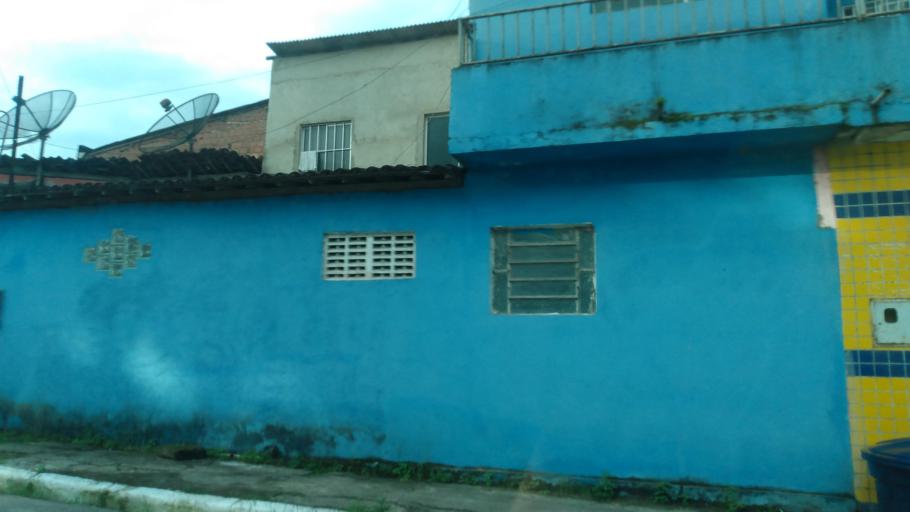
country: BR
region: Pernambuco
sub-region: Palmares
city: Palmares
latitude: -8.6815
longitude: -35.5839
